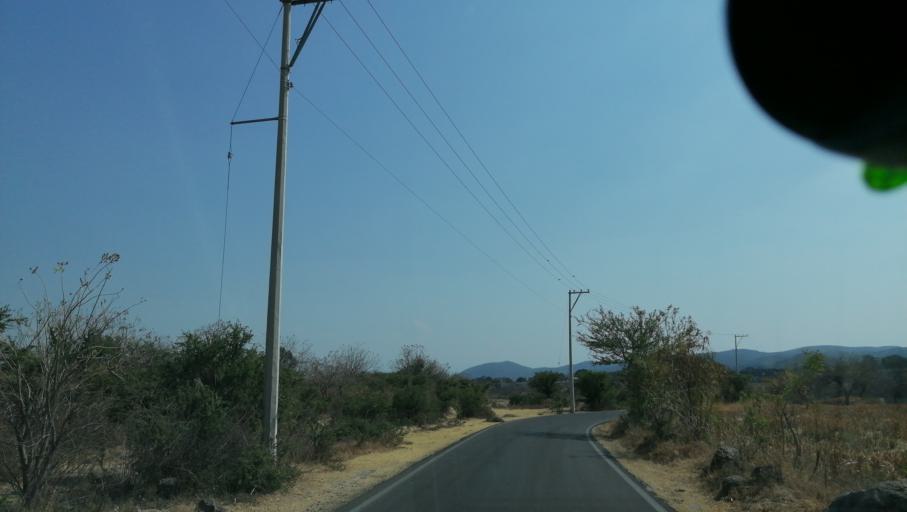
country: MX
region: Puebla
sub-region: Atzitzihuacan
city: San Miguel Aguacomulican
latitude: 18.8292
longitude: -98.5480
